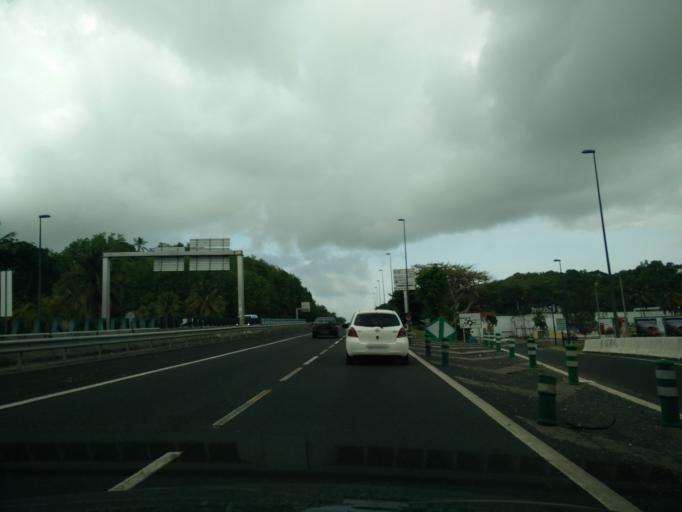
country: GP
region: Guadeloupe
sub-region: Guadeloupe
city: Pointe-a-Pitre
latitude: 16.2199
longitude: -61.5187
